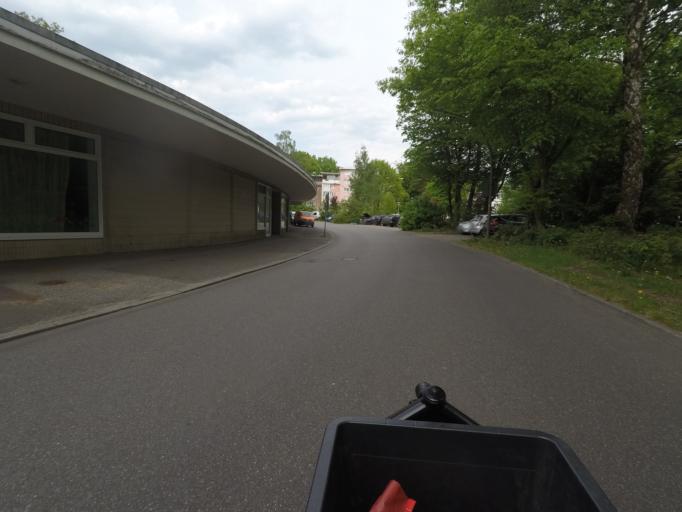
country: DE
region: Hamburg
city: Wellingsbuettel
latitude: 53.6247
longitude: 10.0918
